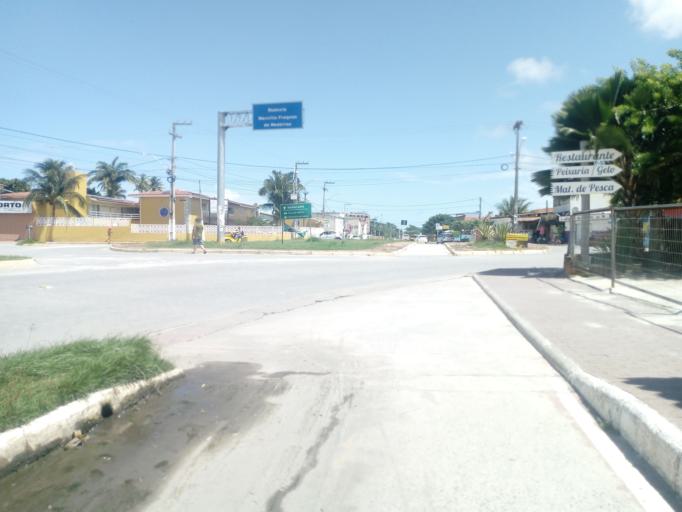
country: BR
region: Pernambuco
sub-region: Ipojuca
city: Ipojuca
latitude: -8.5064
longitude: -35.0081
